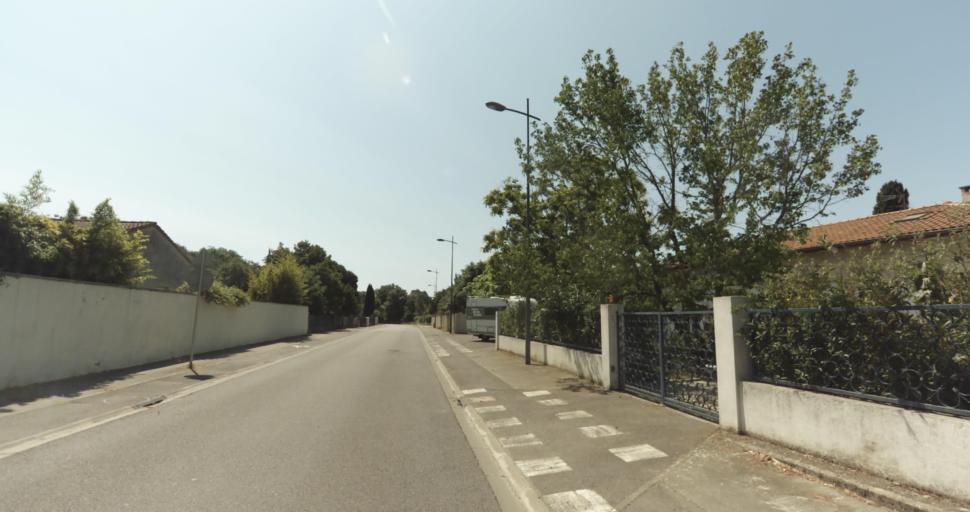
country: FR
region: Midi-Pyrenees
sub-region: Departement de la Haute-Garonne
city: Plaisance-du-Touch
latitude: 43.5764
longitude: 1.2896
